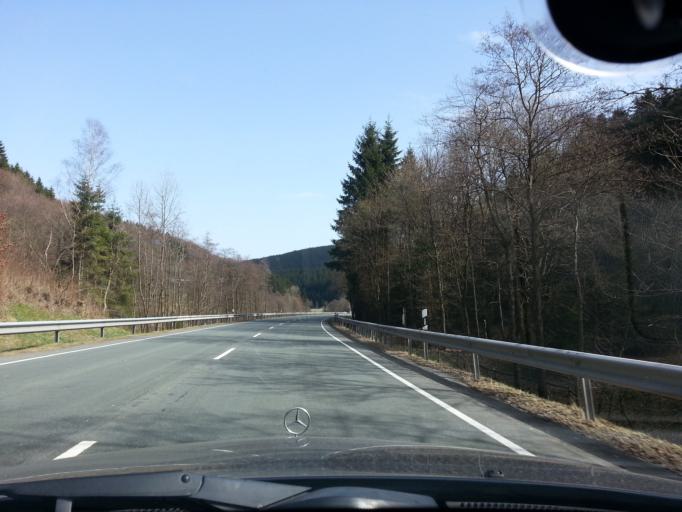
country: DE
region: North Rhine-Westphalia
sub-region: Regierungsbezirk Arnsberg
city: Bad Fredeburg
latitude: 51.2323
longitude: 8.3537
